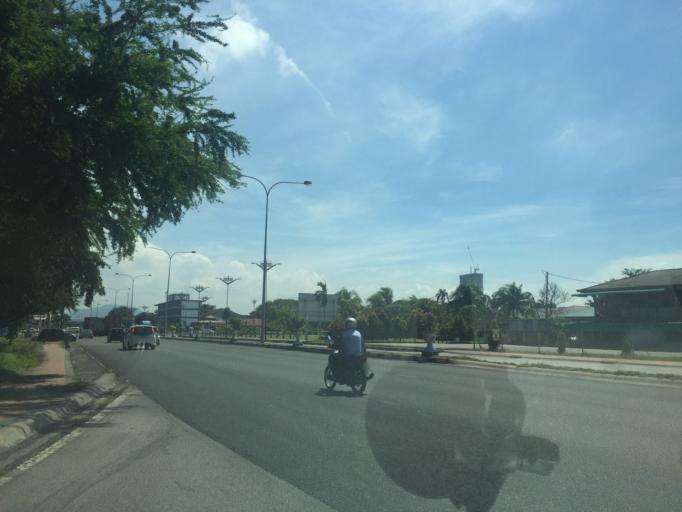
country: MY
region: Penang
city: Butterworth
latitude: 5.4078
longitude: 100.3682
